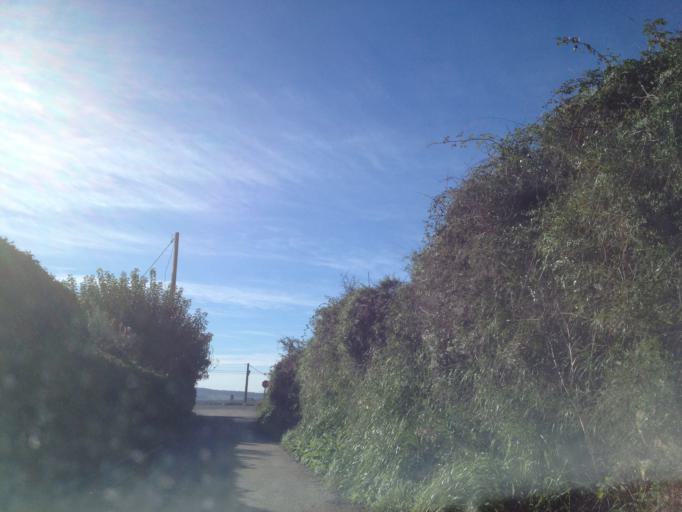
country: ES
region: Balearic Islands
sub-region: Illes Balears
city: Sineu
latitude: 39.6437
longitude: 3.0325
